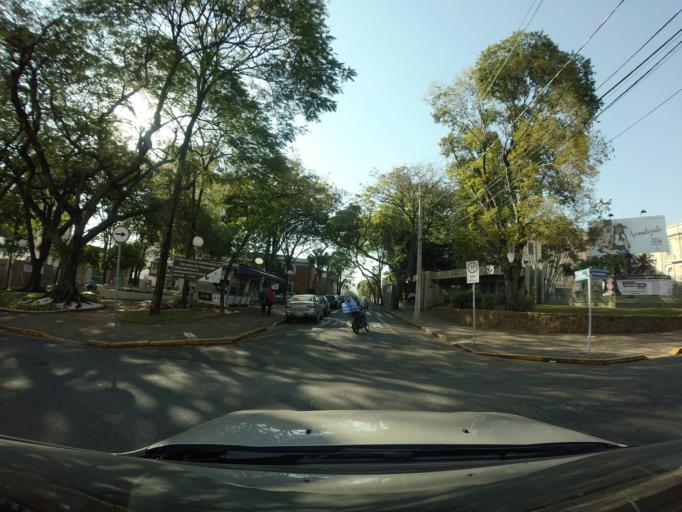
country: BR
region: Sao Paulo
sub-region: Piracicaba
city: Piracicaba
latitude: -22.7319
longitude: -47.6533
